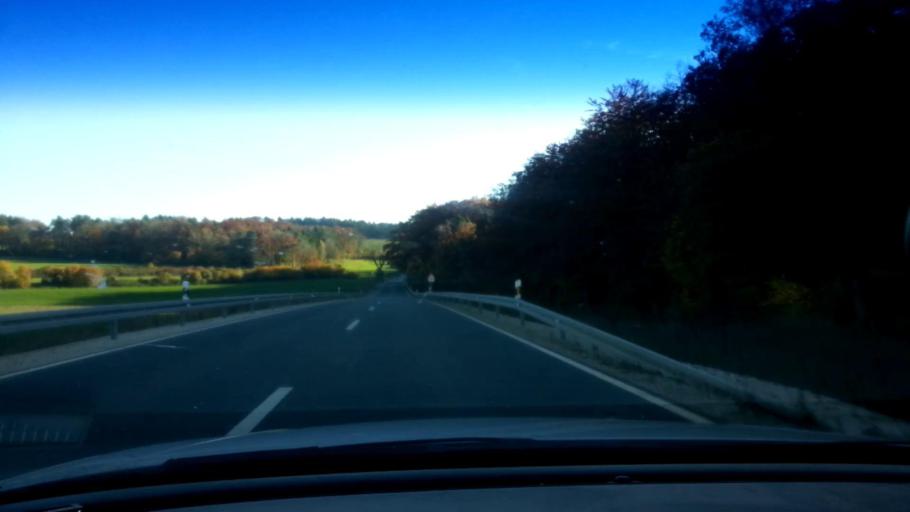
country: DE
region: Bavaria
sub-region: Upper Franconia
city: Poxdorf
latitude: 49.9212
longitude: 11.0889
